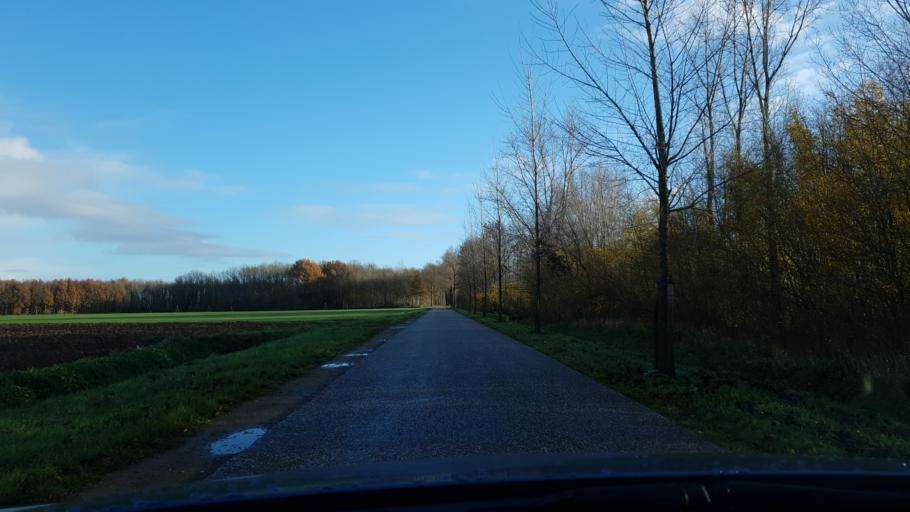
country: NL
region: Gelderland
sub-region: Gemeente Wijchen
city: Bergharen
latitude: 51.8413
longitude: 5.6603
